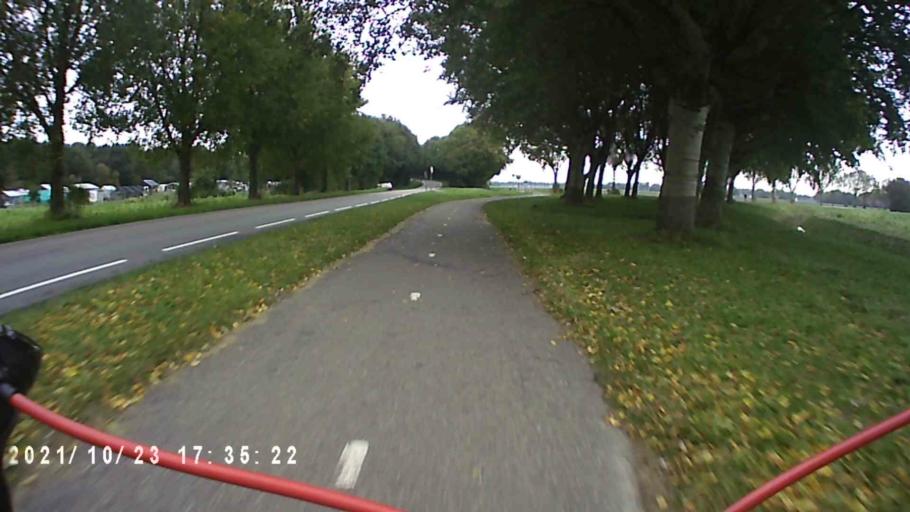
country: NL
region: North Holland
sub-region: Gemeente Hollands Kroon
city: Den Oever
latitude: 52.8652
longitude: 5.0238
